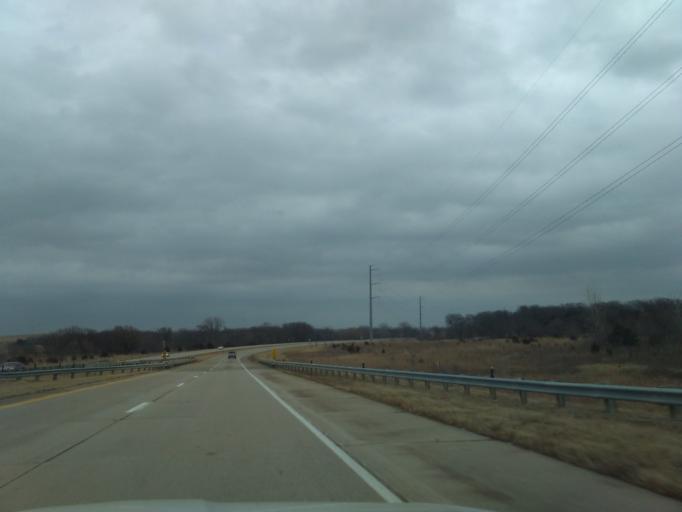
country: US
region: Nebraska
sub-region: Otoe County
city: Syracuse
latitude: 40.6761
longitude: -96.0407
